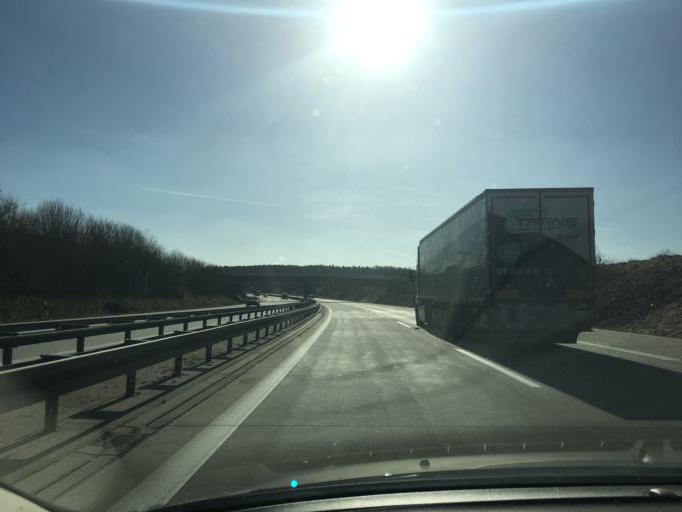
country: DE
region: Saxony
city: Muhlau
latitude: 50.8867
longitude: 12.7540
